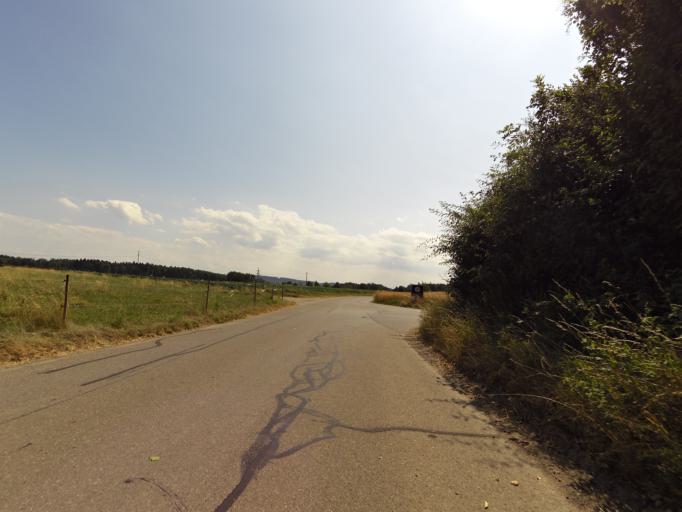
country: CH
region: Aargau
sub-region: Bezirk Baden
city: Birmenstorf
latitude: 47.4553
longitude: 8.2611
